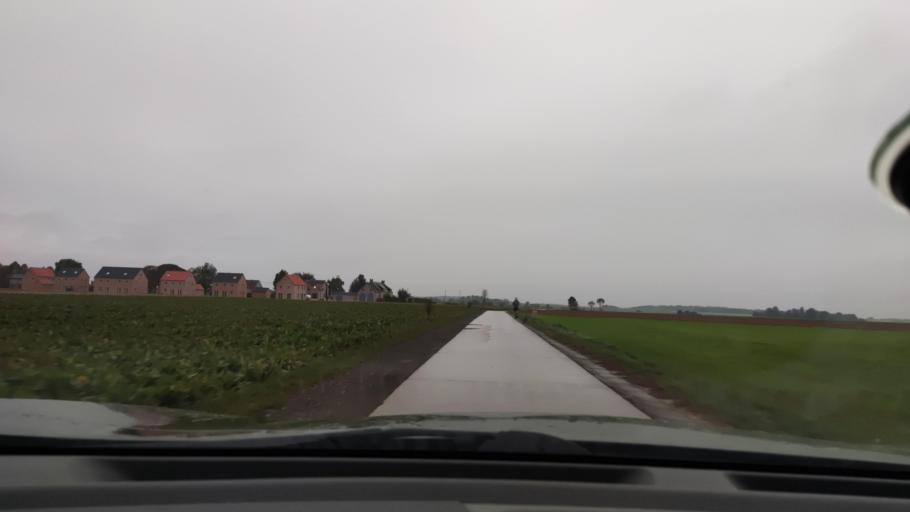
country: BE
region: Wallonia
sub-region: Province du Brabant Wallon
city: Beauvechain
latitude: 50.7685
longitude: 4.8053
